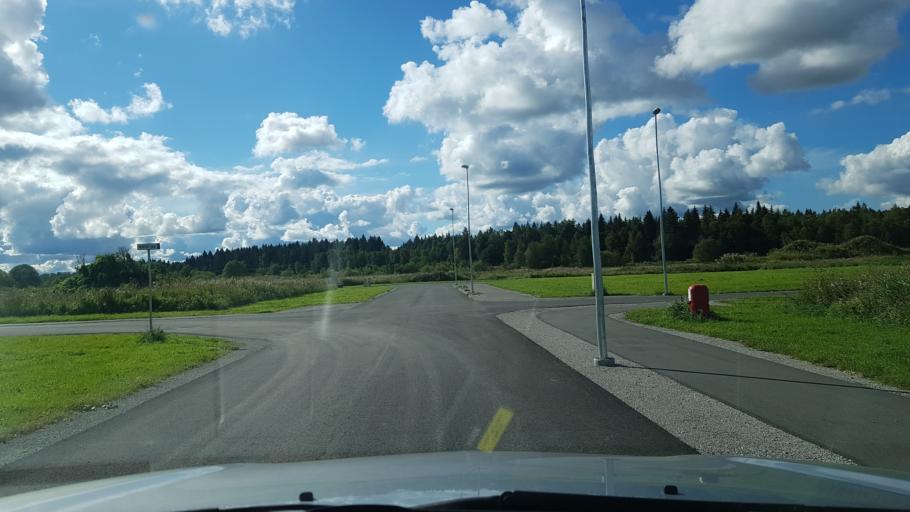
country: EE
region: Harju
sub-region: Kiili vald
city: Kiili
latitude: 59.3585
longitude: 24.8244
